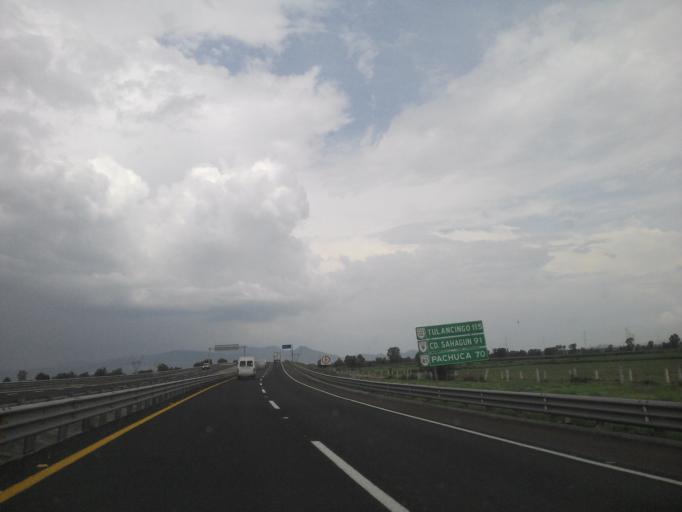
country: MX
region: Hidalgo
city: Doxey
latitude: 20.0985
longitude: -99.2791
